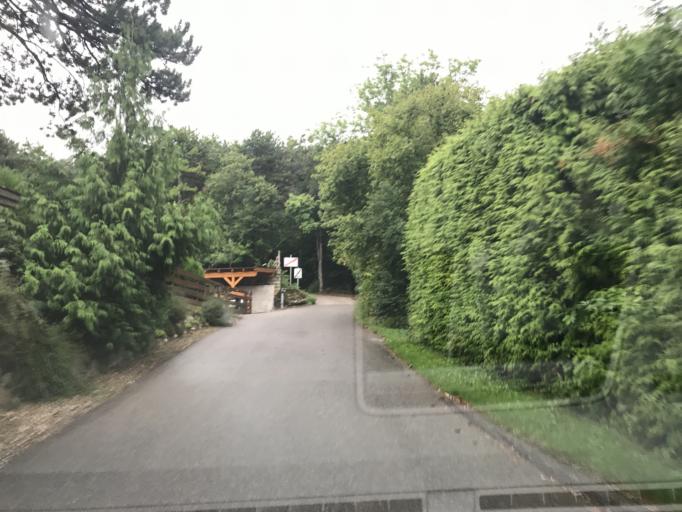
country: AT
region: Lower Austria
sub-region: Politischer Bezirk Wiener Neustadt
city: Markt Piesting
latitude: 47.8584
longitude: 16.1740
